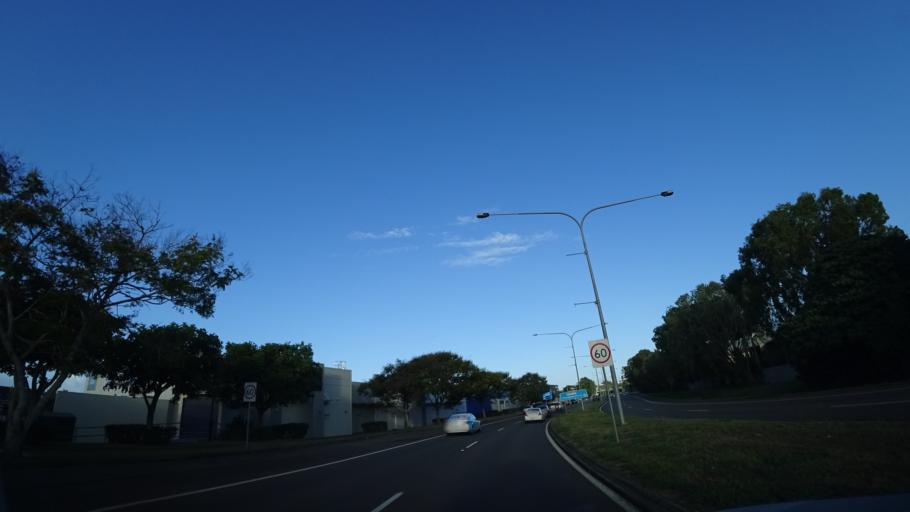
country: AU
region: Queensland
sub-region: Sunshine Coast
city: Buderim
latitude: -26.6519
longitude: 153.0799
